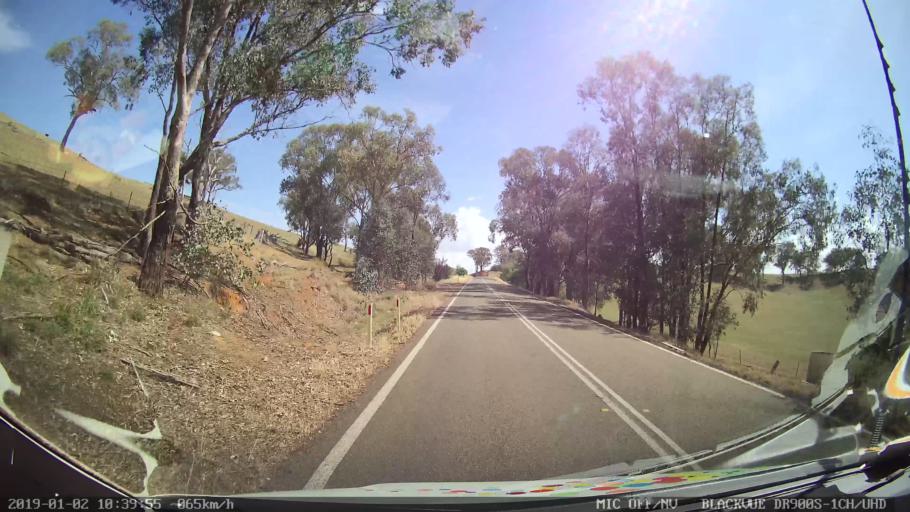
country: AU
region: New South Wales
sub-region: Gundagai
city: Gundagai
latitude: -34.8066
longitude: 148.3175
